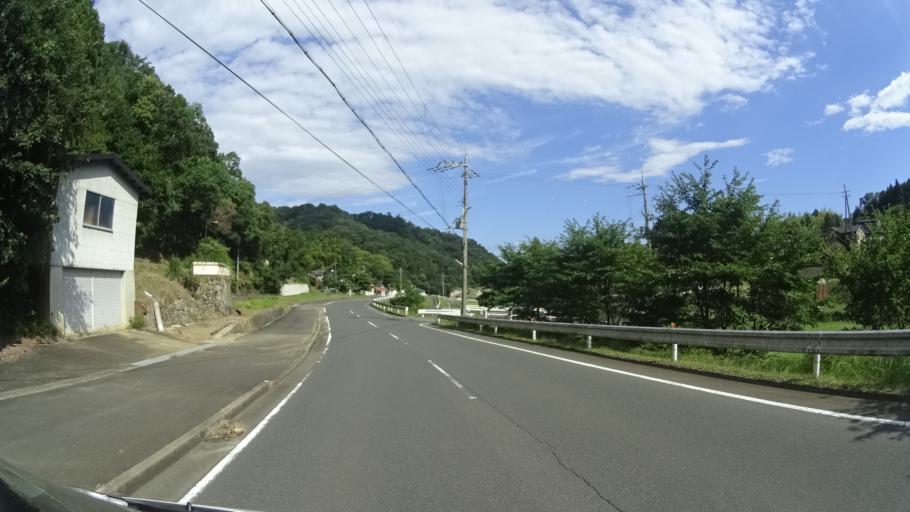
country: JP
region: Kyoto
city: Fukuchiyama
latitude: 35.3409
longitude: 135.1653
